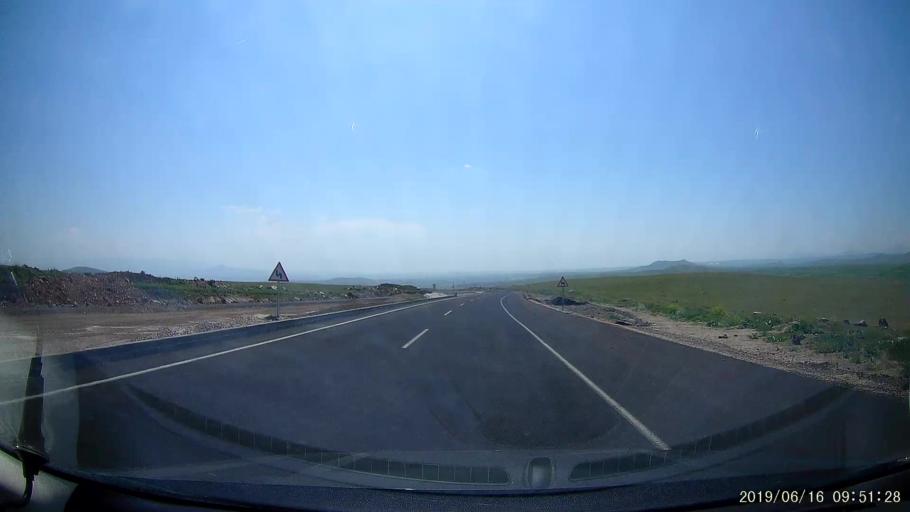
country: TR
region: Kars
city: Digor
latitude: 40.3913
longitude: 43.3675
